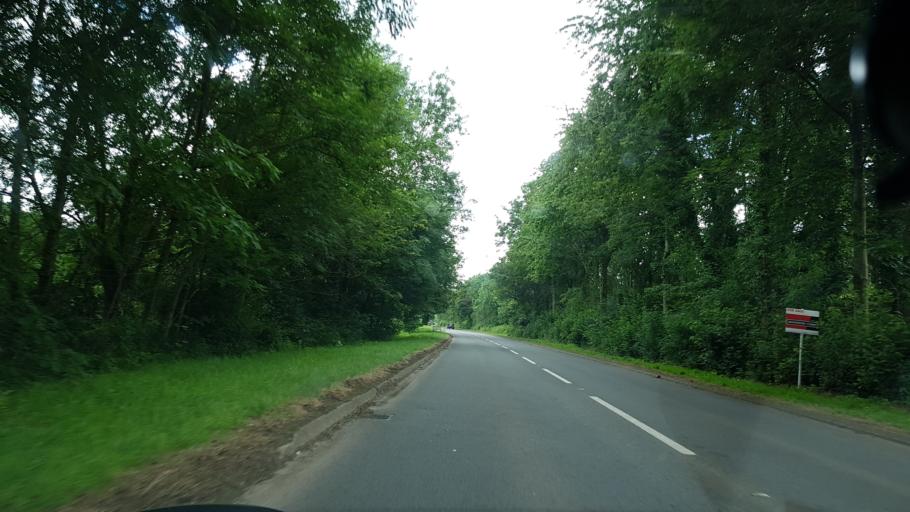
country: GB
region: England
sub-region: Herefordshire
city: Llancillo
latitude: 51.8803
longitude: -2.9793
